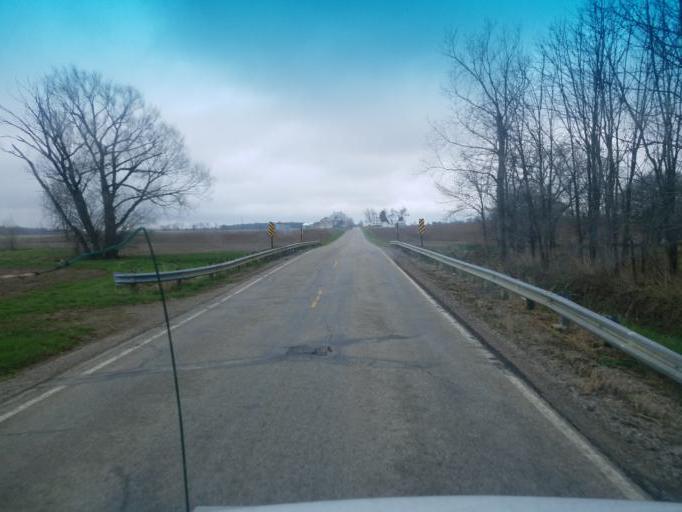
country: US
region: Ohio
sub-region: Richland County
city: Shelby
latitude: 40.9014
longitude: -82.6258
